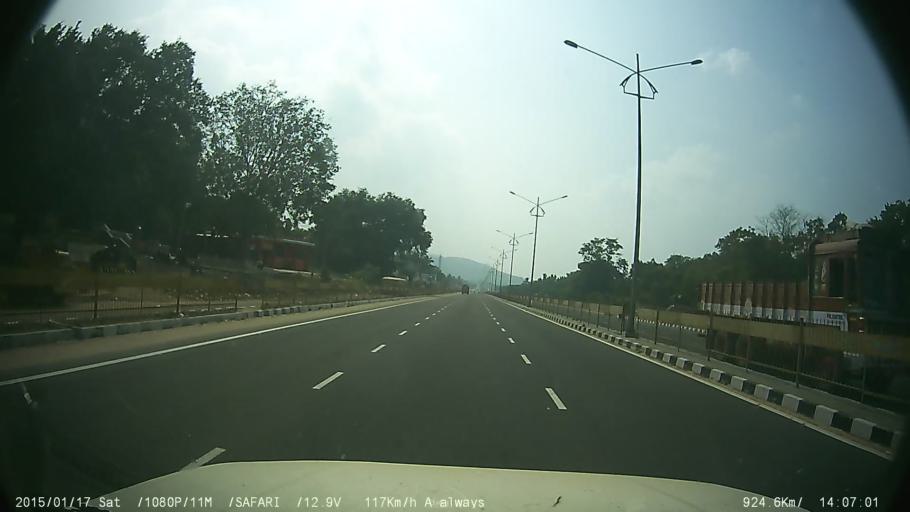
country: IN
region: Tamil Nadu
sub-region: Vellore
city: Ambur
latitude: 12.8337
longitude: 78.7833
